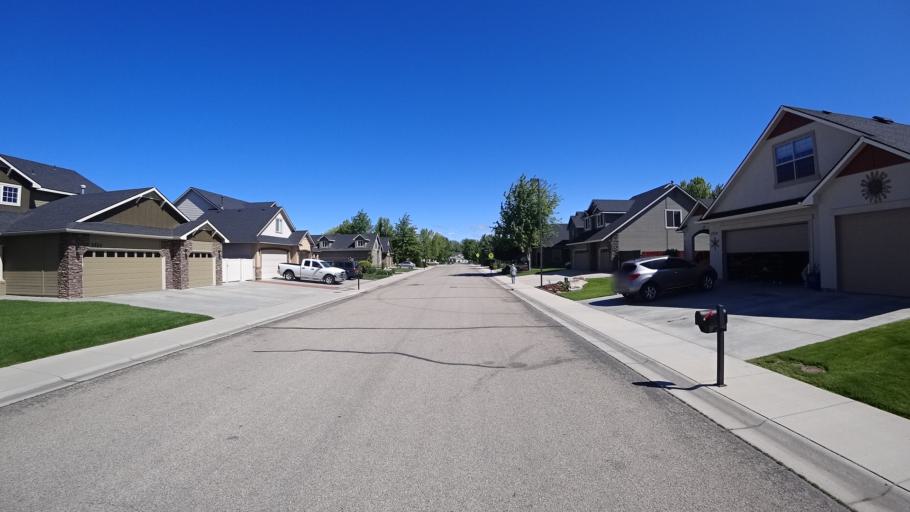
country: US
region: Idaho
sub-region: Ada County
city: Meridian
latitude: 43.6384
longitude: -116.3665
